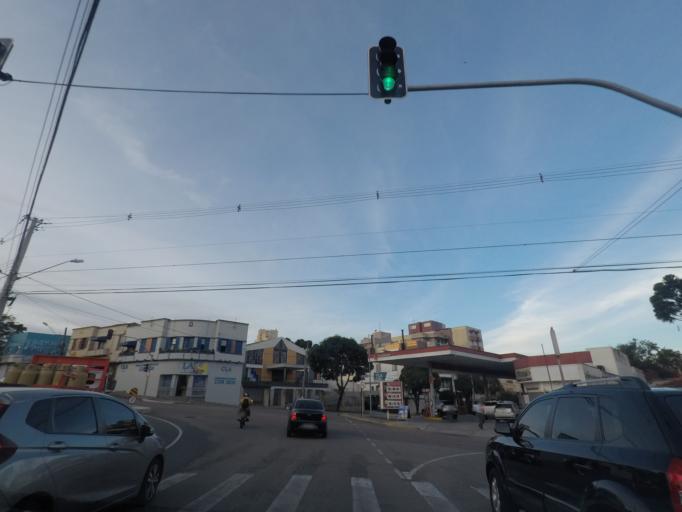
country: BR
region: Parana
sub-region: Curitiba
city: Curitiba
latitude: -25.4220
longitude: -49.2747
